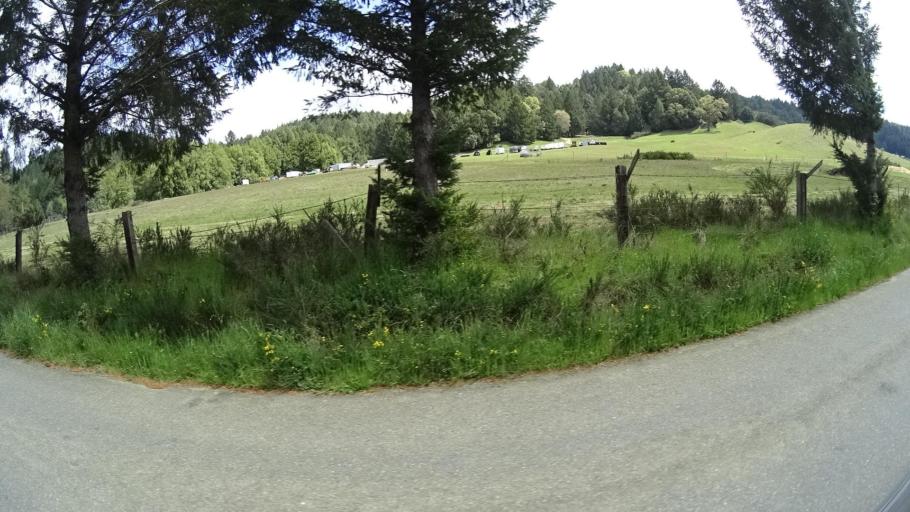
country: US
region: California
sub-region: Humboldt County
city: Redway
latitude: 40.0420
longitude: -123.9593
